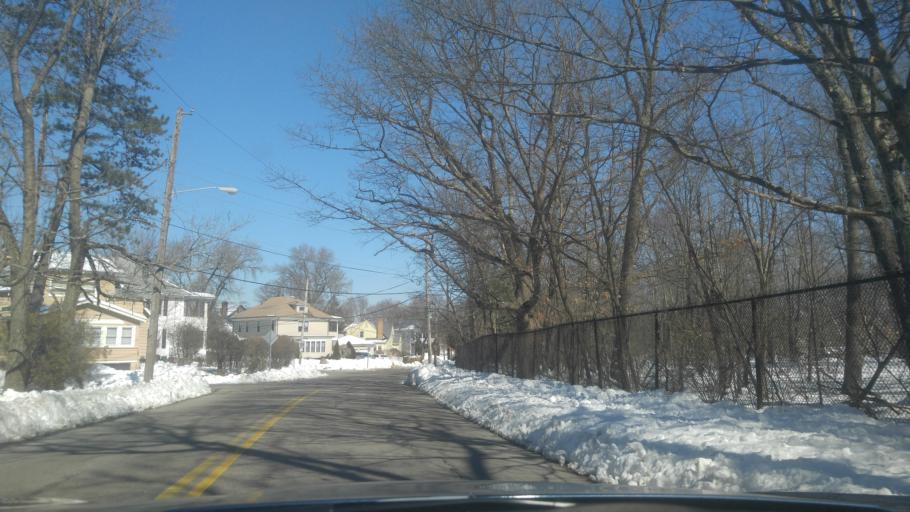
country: US
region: Rhode Island
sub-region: Providence County
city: Pawtucket
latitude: 41.8614
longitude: -71.3838
